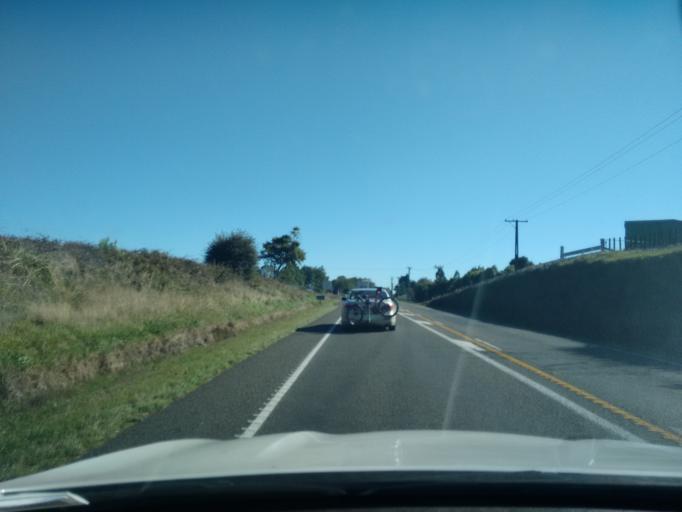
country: NZ
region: Taranaki
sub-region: South Taranaki District
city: Eltham
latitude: -39.2383
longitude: 174.2455
